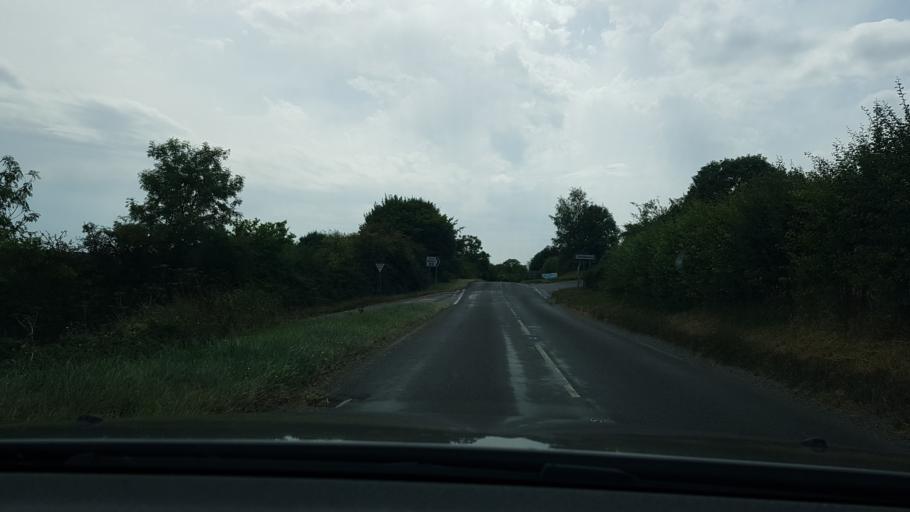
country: GB
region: England
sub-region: Wiltshire
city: Shalbourne
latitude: 51.3630
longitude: -1.5621
